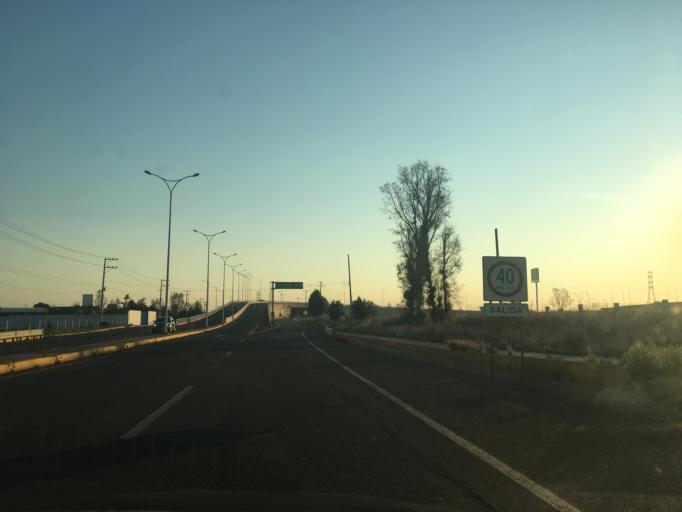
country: MX
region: Zacatecas
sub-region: Calera
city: Victor Rosales
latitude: 22.9107
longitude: -102.6734
